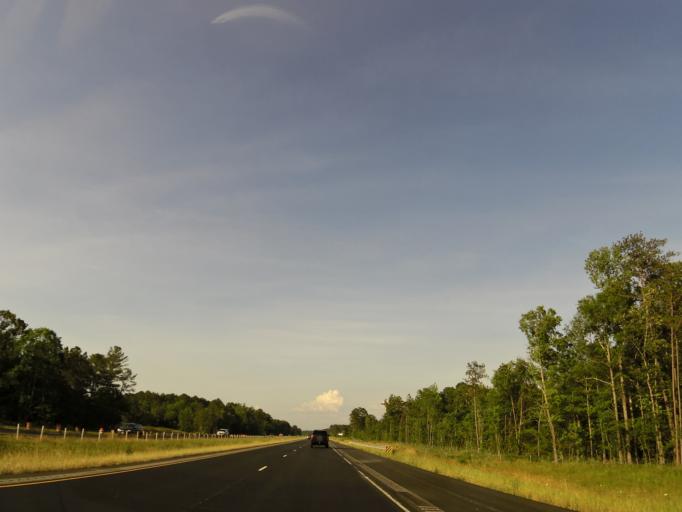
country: US
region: Alabama
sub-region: Etowah County
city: Attalla
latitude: 33.9694
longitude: -86.1189
